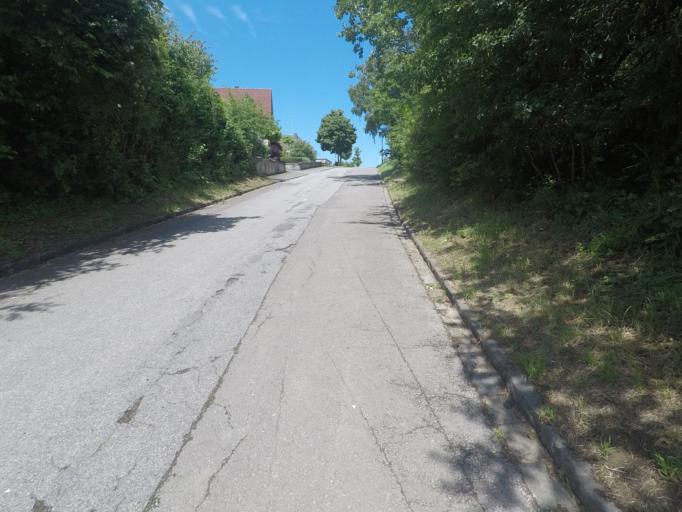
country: LU
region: Luxembourg
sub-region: Canton de Luxembourg
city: Luxembourg
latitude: 49.5862
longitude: 6.1092
